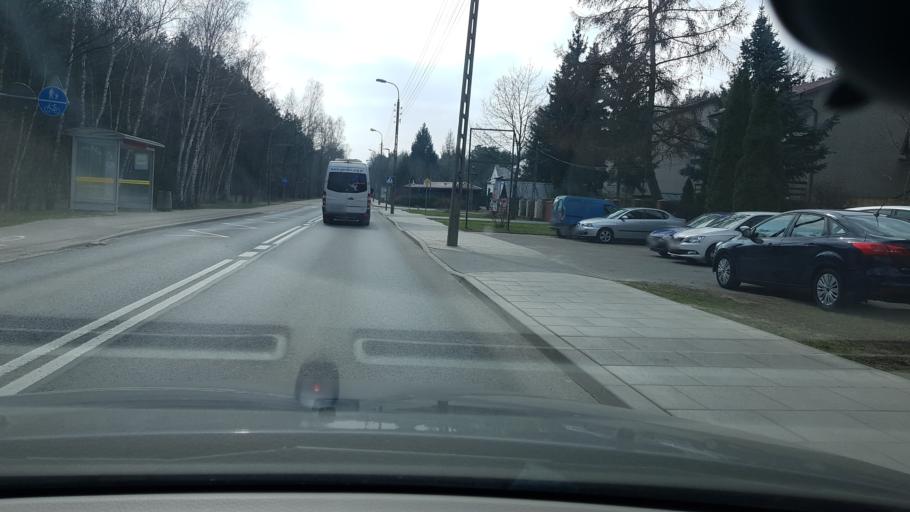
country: PL
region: Masovian Voivodeship
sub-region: Warszawa
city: Wesola
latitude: 52.2430
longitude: 21.2228
